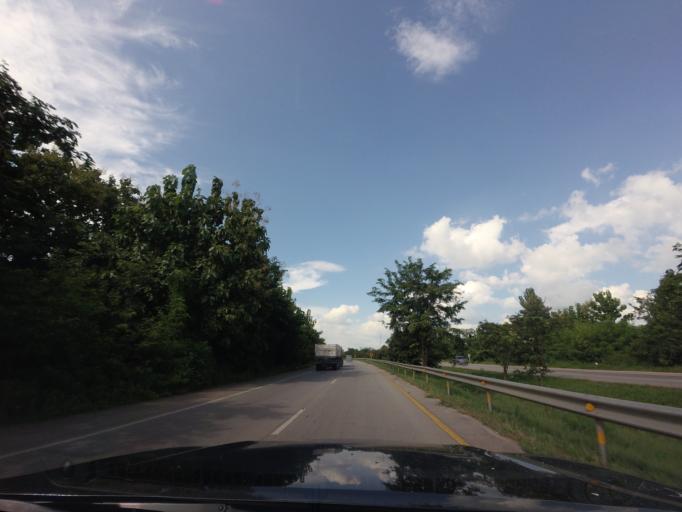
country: TH
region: Nong Khai
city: Sa Khrai
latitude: 17.6564
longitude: 102.7899
